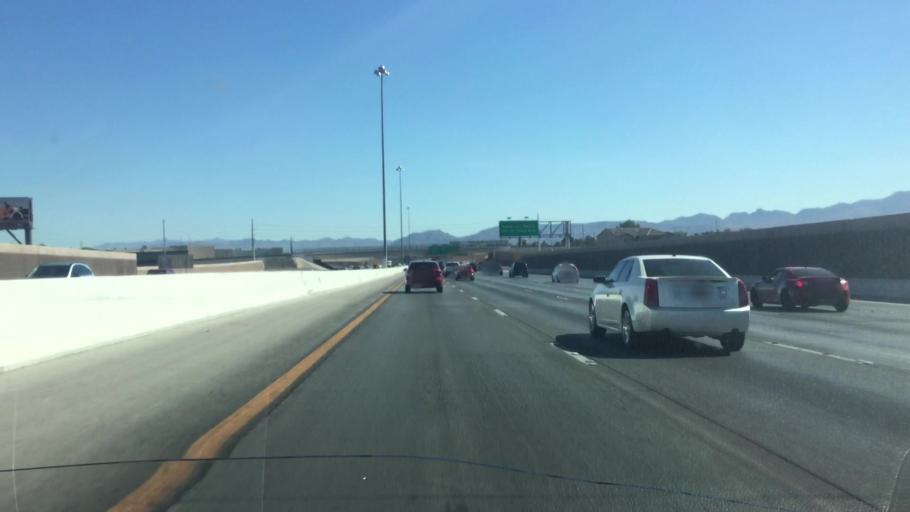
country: US
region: Nevada
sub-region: Clark County
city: Paradise
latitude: 36.0676
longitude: -115.1943
